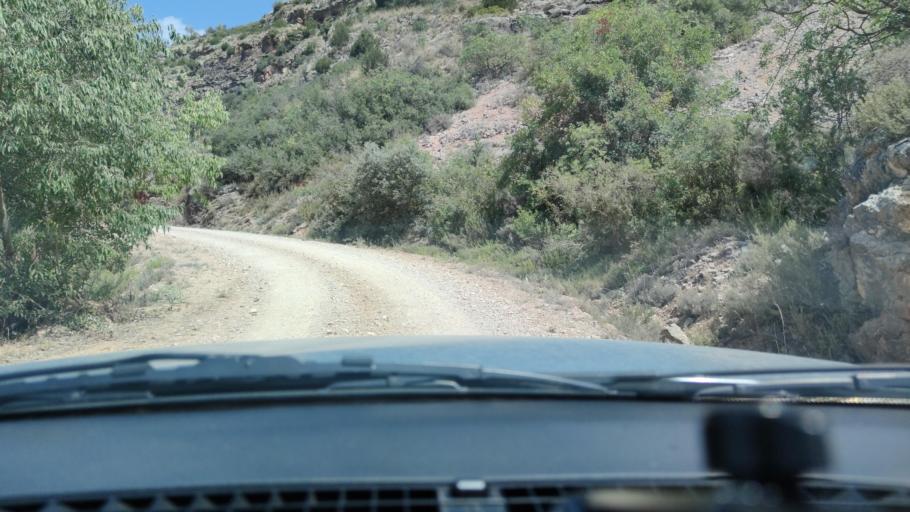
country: ES
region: Catalonia
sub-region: Provincia de Lleida
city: Camarasa
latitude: 41.9274
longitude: 0.8216
